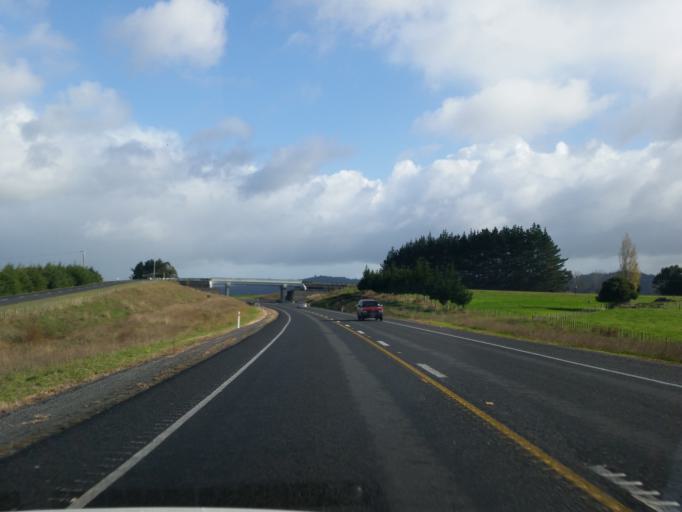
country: NZ
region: Waikato
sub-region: Waikato District
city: Te Kauwhata
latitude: -37.2218
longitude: 175.1413
